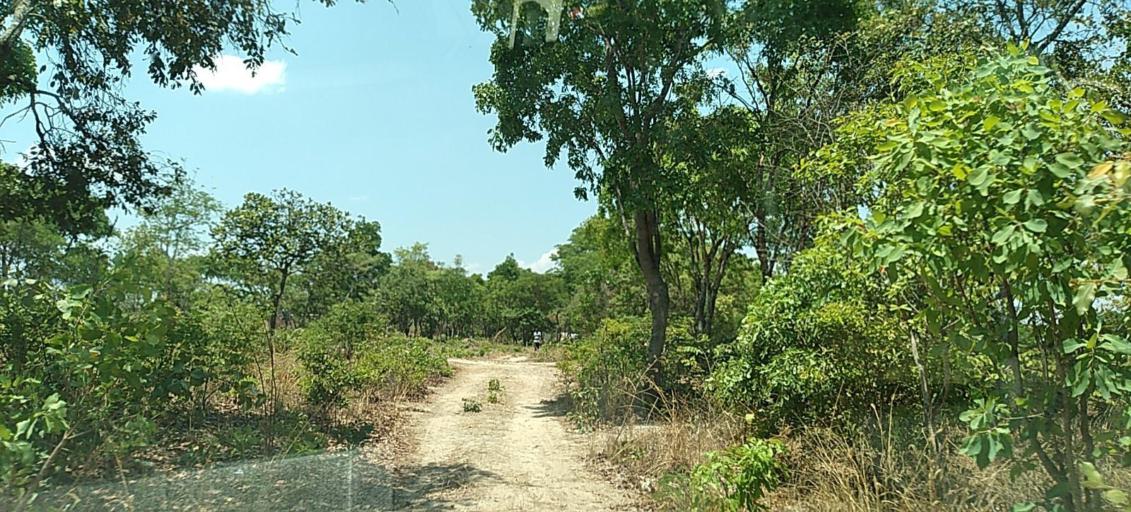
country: ZM
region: Central
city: Kapiri Mposhi
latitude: -13.6731
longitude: 28.5034
